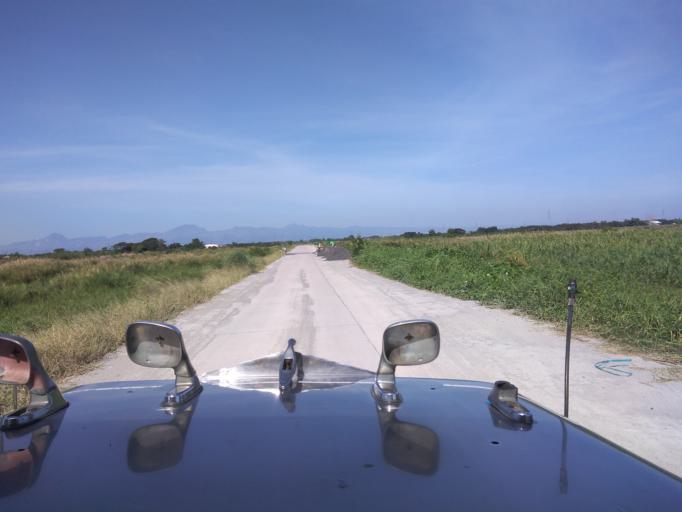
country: PH
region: Central Luzon
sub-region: Province of Pampanga
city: Bacolor
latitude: 14.9933
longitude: 120.6709
